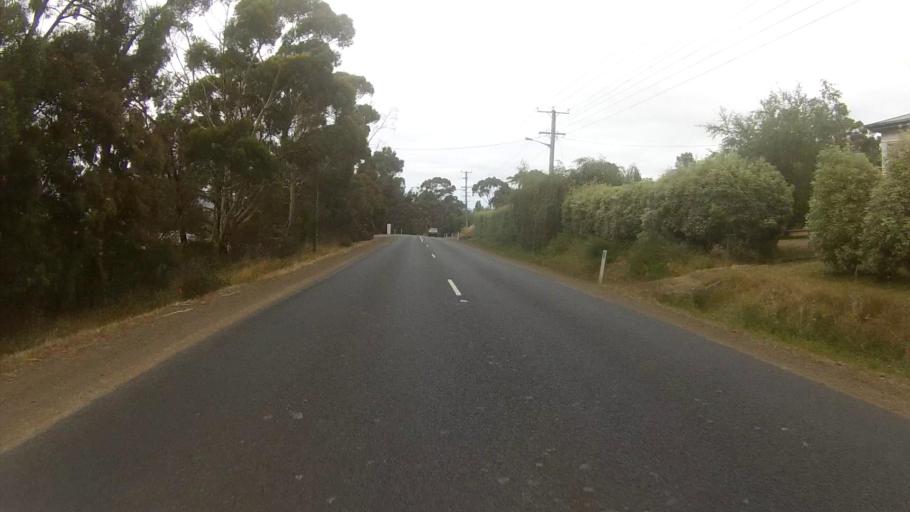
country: AU
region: Tasmania
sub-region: Kingborough
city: Margate
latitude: -43.0164
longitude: 147.2517
